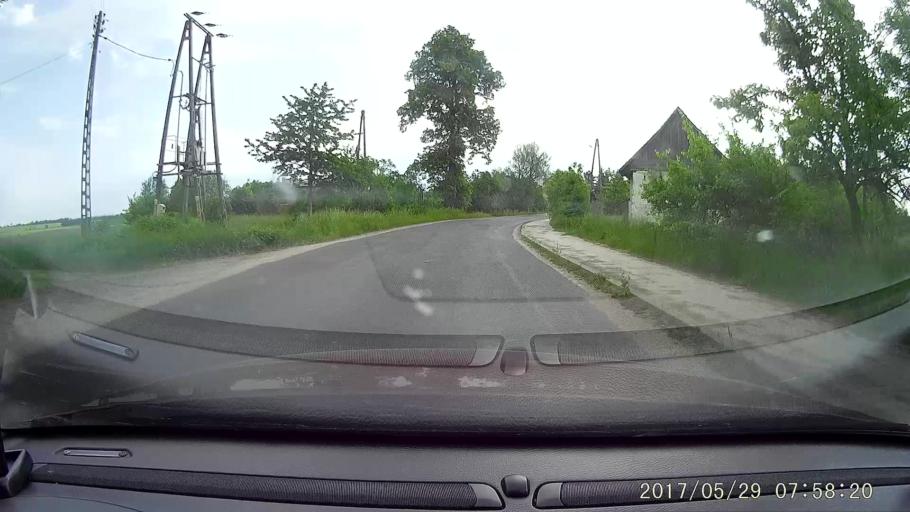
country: PL
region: Lower Silesian Voivodeship
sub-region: Powiat zlotoryjski
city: Olszanica
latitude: 51.2010
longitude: 15.7849
